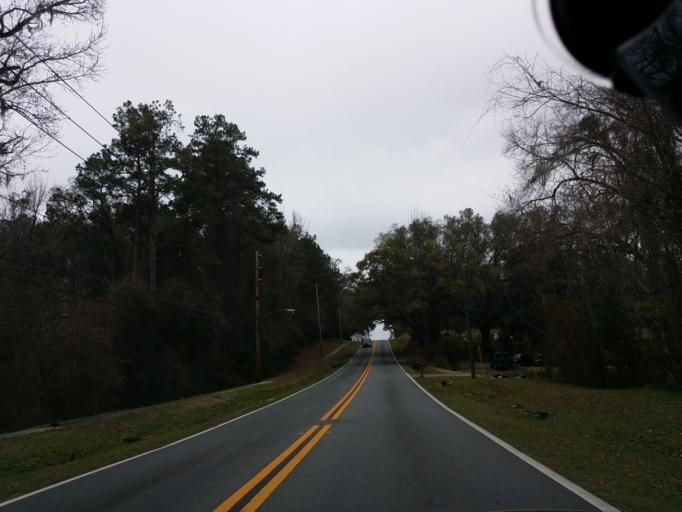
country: US
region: Florida
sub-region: Leon County
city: Tallahassee
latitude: 30.4978
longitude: -84.2299
